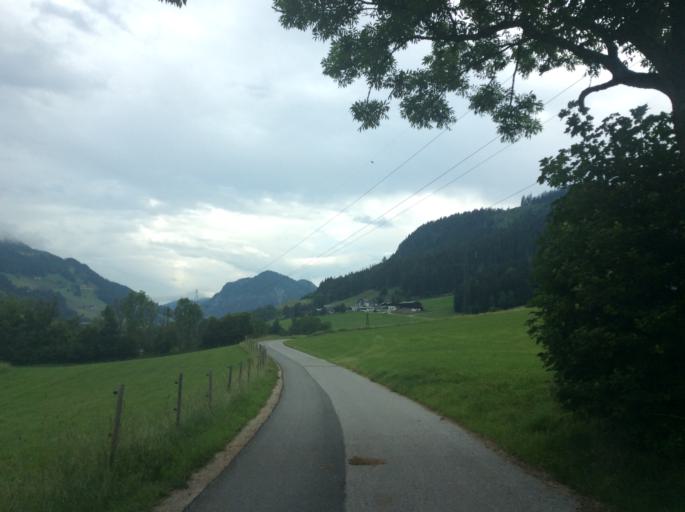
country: AT
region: Styria
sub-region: Politischer Bezirk Liezen
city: Schladming
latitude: 47.3900
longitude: 13.6485
